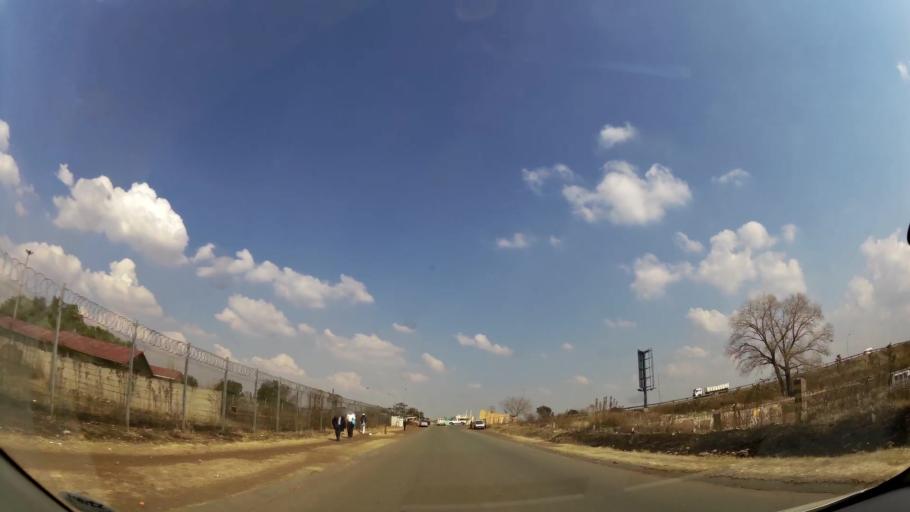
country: ZA
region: Gauteng
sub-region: Ekurhuleni Metropolitan Municipality
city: Germiston
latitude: -26.3256
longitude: 28.1412
